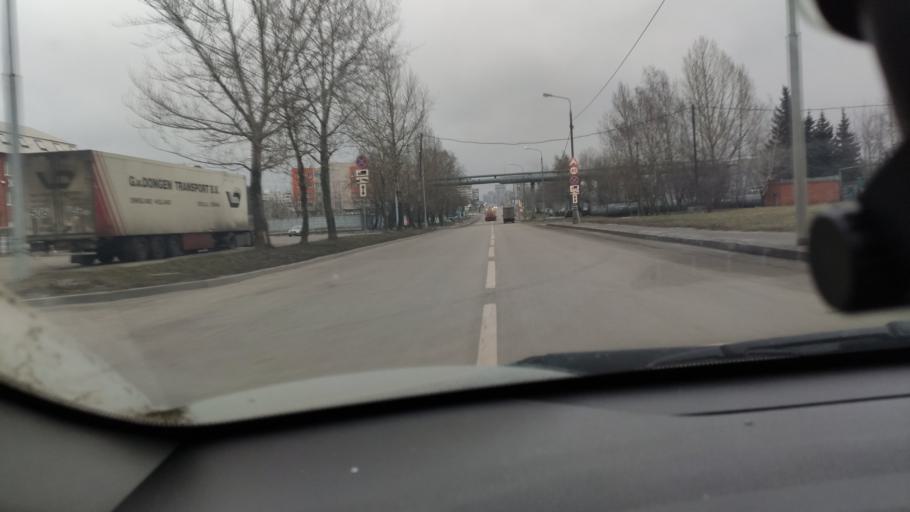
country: RU
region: Moskovskaya
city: Biryulevo Zapadnoye
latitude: 55.5812
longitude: 37.6321
